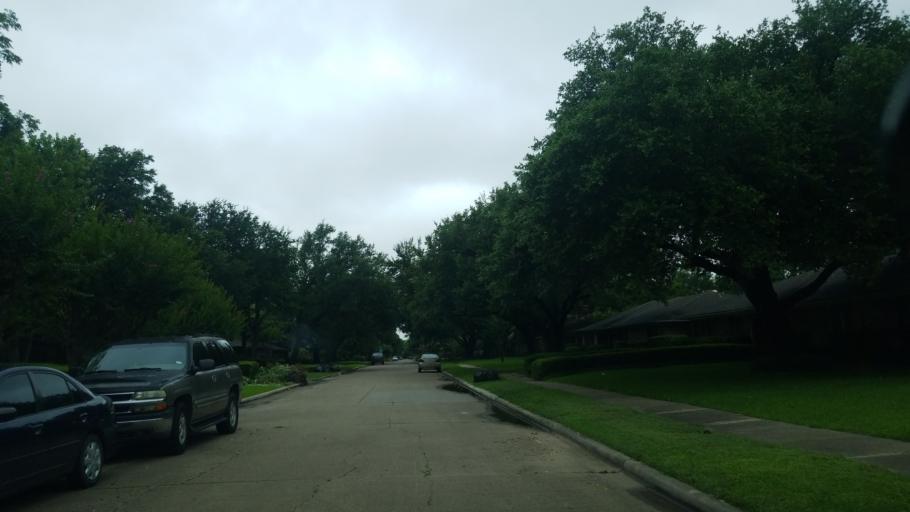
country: US
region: Texas
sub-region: Dallas County
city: Farmers Branch
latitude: 32.8922
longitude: -96.8713
